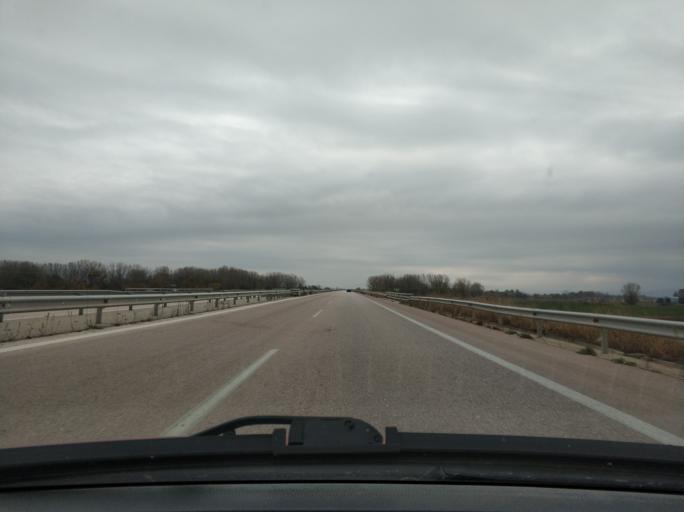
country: GR
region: Central Macedonia
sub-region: Nomos Thessalonikis
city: Kavallari
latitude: 40.7308
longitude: 23.0561
